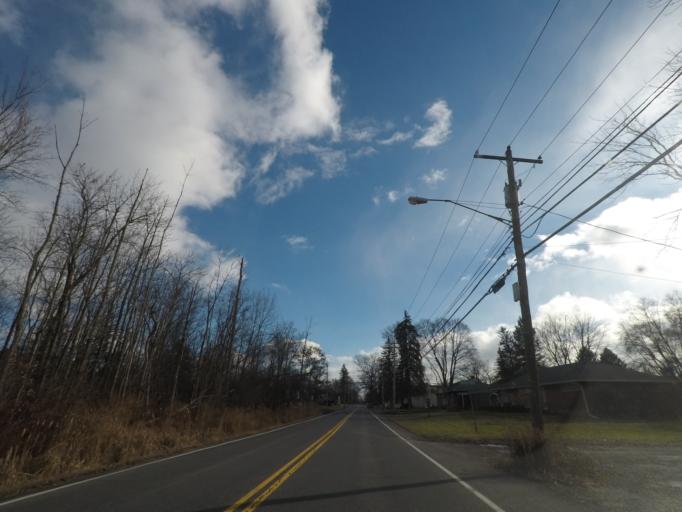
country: US
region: New York
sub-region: Schenectady County
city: Niskayuna
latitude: 42.7642
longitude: -73.8904
